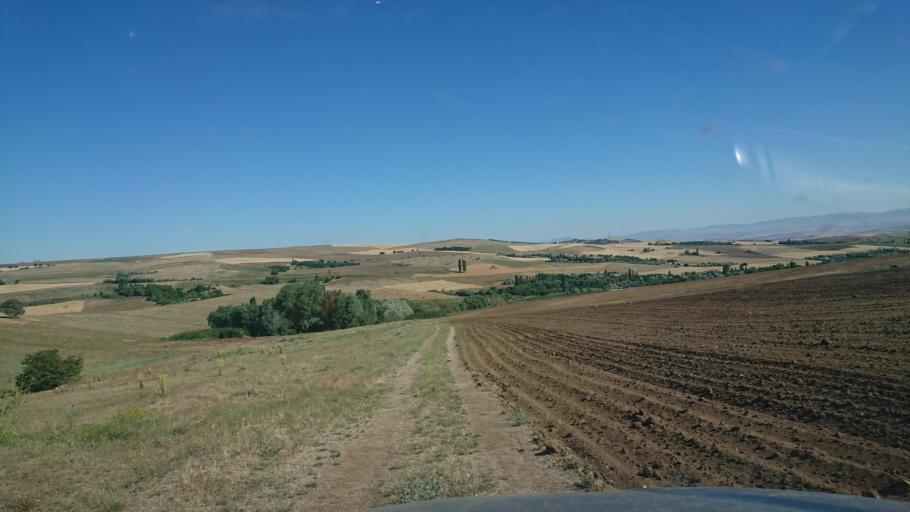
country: TR
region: Aksaray
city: Agacoren
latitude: 38.8404
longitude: 33.9326
